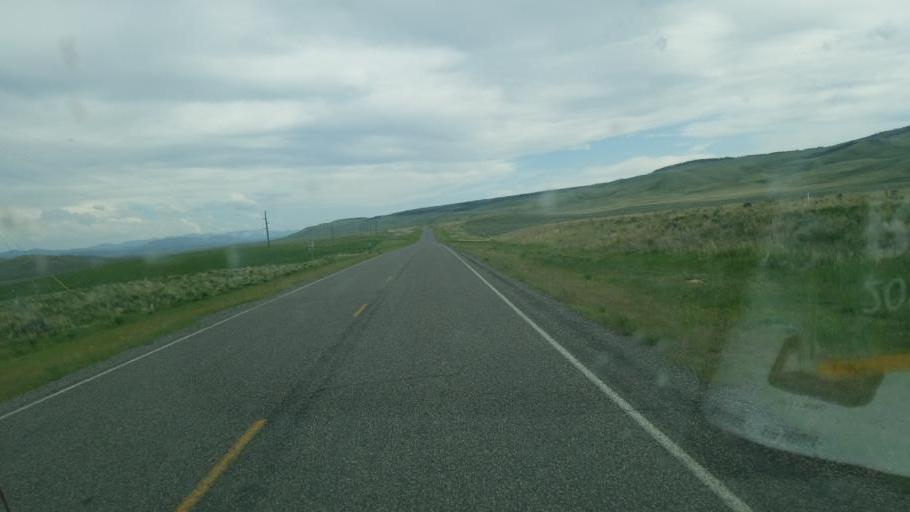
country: US
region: Montana
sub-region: Meagher County
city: White Sulphur Springs
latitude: 46.3923
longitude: -110.8805
